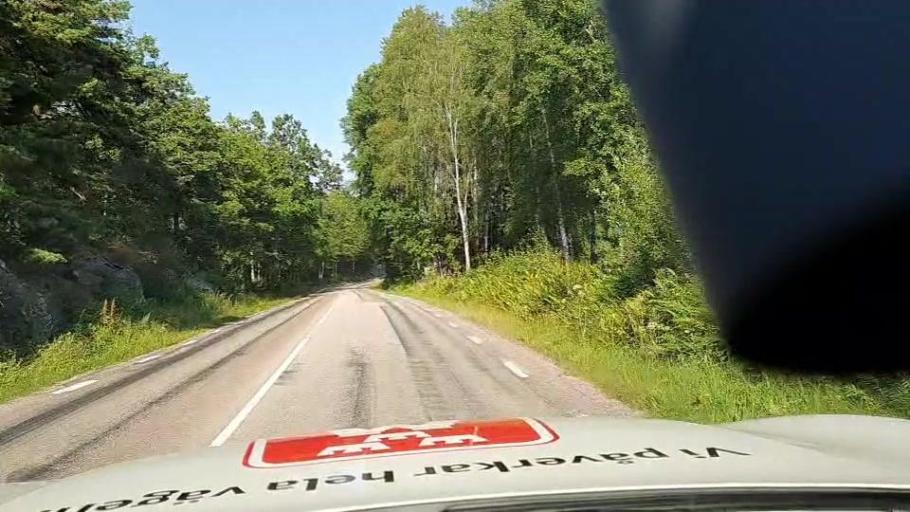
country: SE
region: Vaestra Goetaland
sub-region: Orust
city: Henan
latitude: 58.2104
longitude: 11.5646
